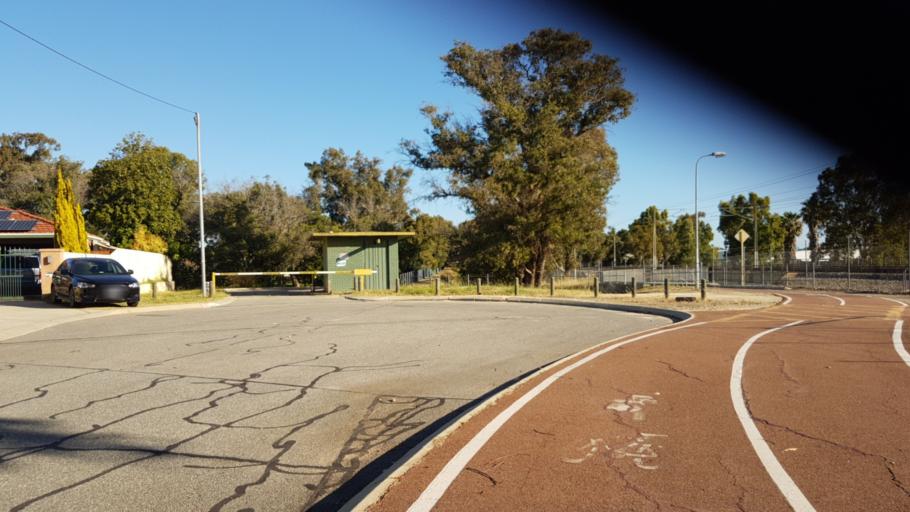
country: AU
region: Western Australia
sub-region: Gosnells
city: Kenwick
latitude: -32.0401
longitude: 115.9734
